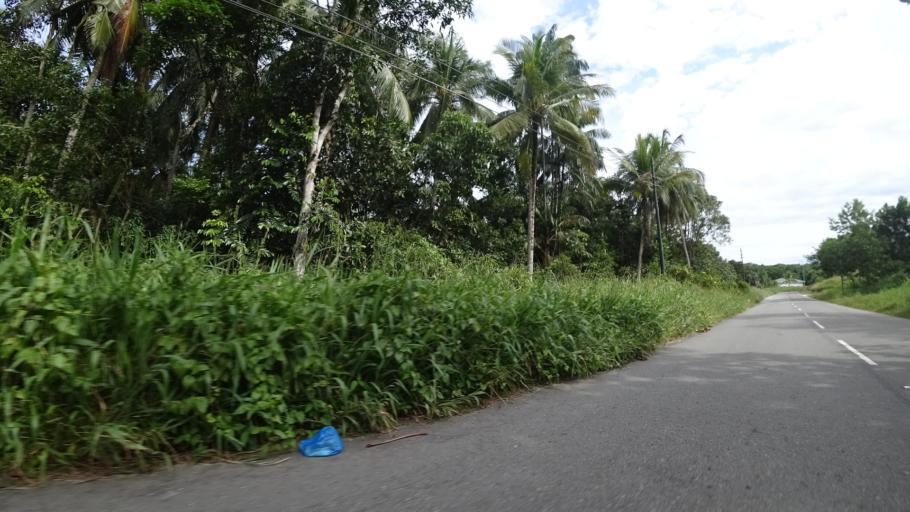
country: BN
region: Brunei and Muara
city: Bandar Seri Begawan
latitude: 4.8539
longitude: 114.9540
